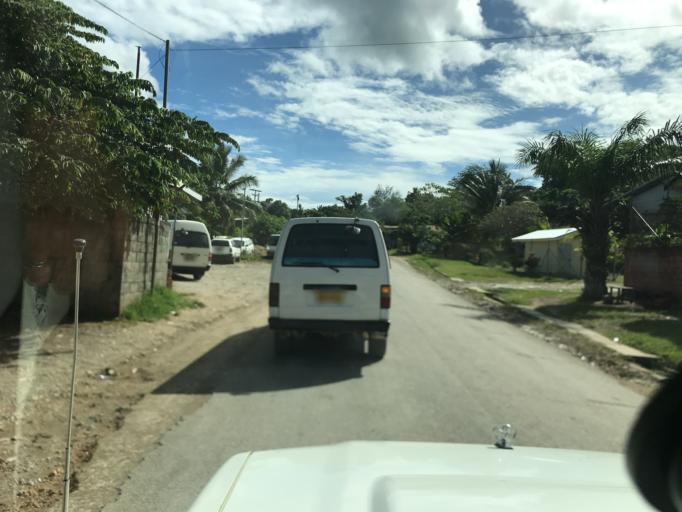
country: SB
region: Malaita
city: Auki
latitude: -8.7683
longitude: 160.6970
